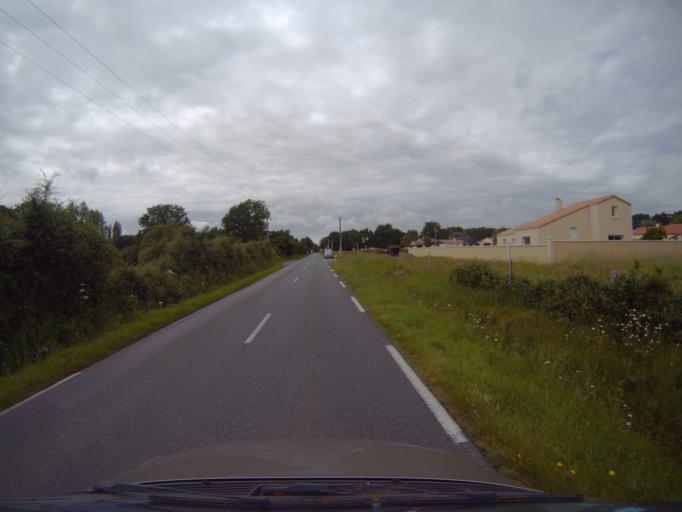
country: FR
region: Pays de la Loire
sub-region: Departement de la Loire-Atlantique
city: Geneston
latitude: 47.0602
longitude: -1.5371
